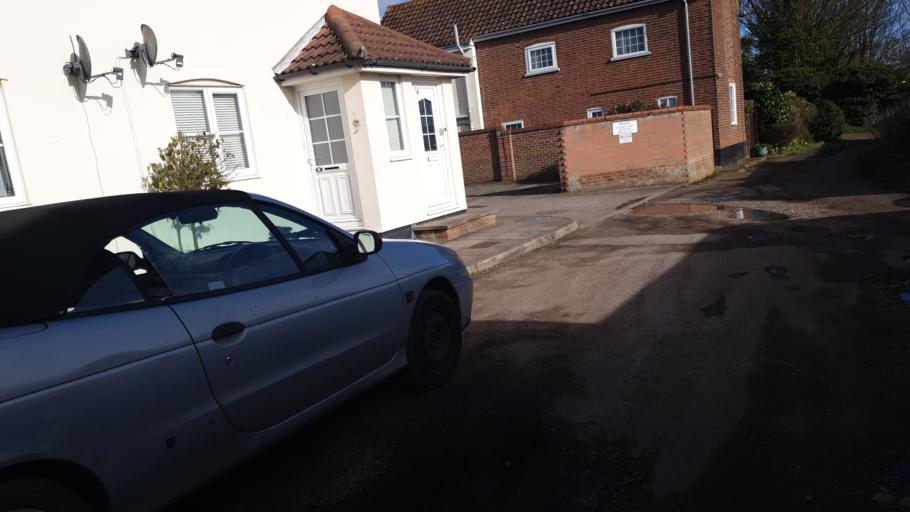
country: GB
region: England
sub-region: Essex
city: Brightlingsea
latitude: 51.8100
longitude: 1.0280
